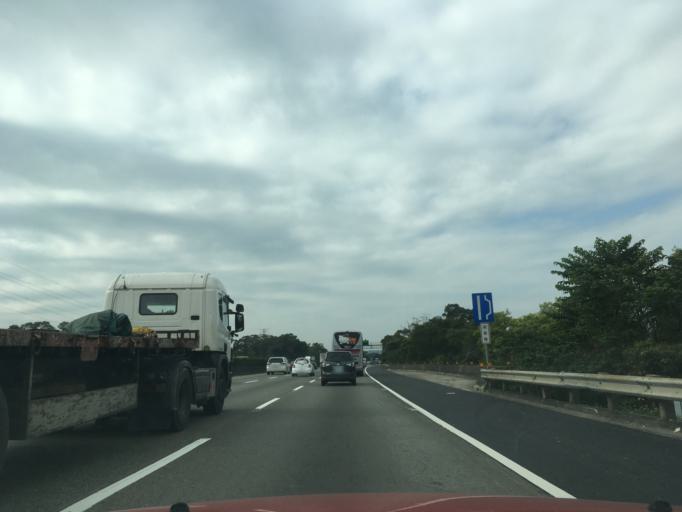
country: TW
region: Taiwan
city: Daxi
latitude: 24.8660
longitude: 121.2347
